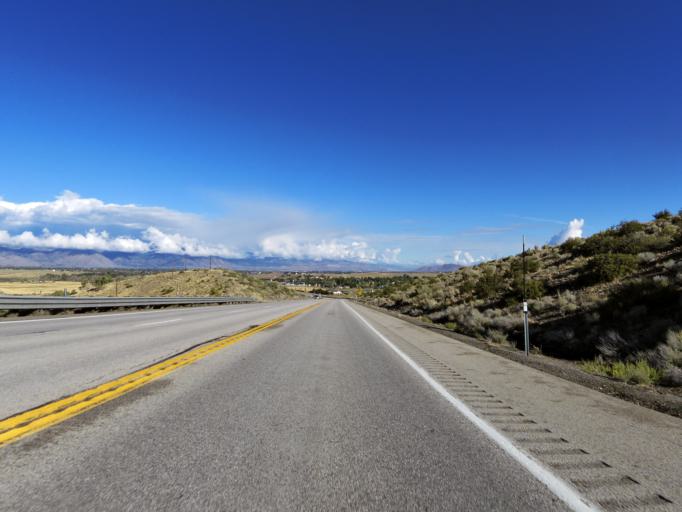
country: US
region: Nevada
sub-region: Douglas County
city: Gardnerville Ranchos
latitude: 38.8746
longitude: -119.6845
